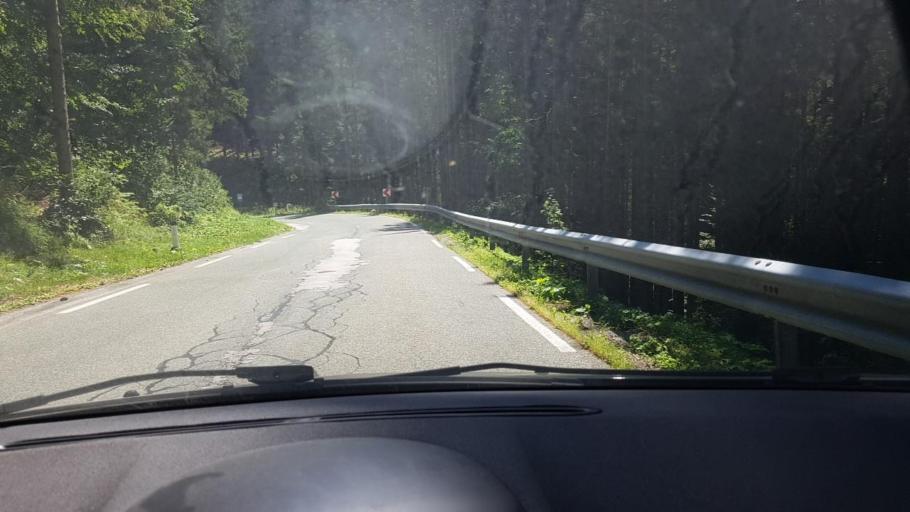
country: SI
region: Jezersko
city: Zgornje Jezersko
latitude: 46.4131
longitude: 14.5304
